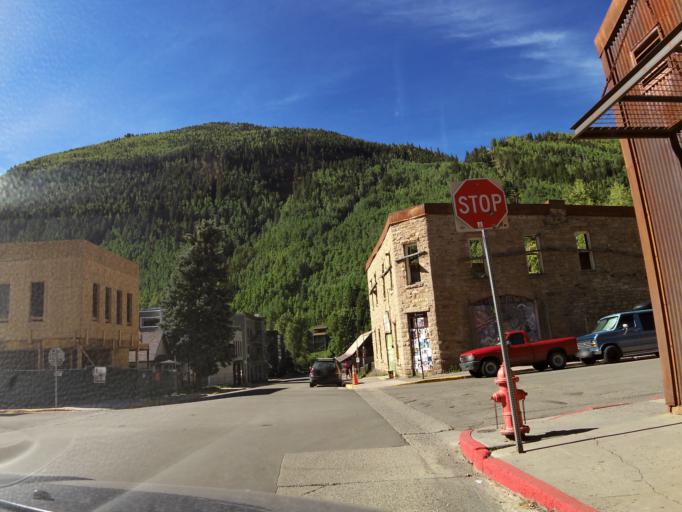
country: US
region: Colorado
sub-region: San Miguel County
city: Telluride
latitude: 37.9367
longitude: -107.8121
